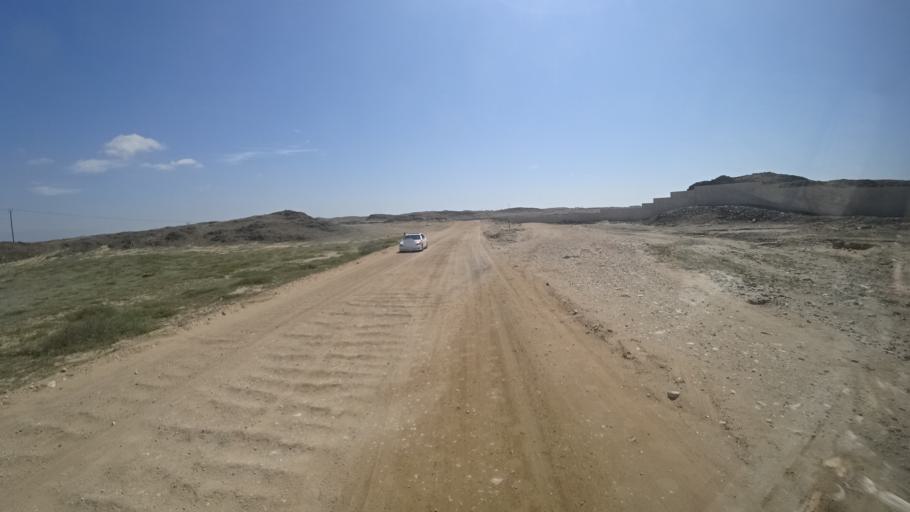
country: OM
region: Zufar
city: Salalah
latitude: 16.9641
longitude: 54.7763
